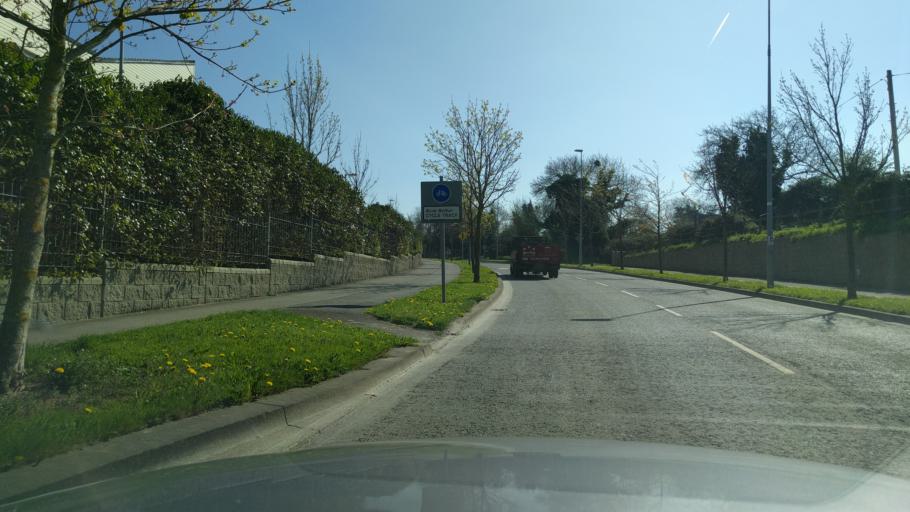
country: IE
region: Leinster
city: Firhouse
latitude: 53.2690
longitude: -6.3383
